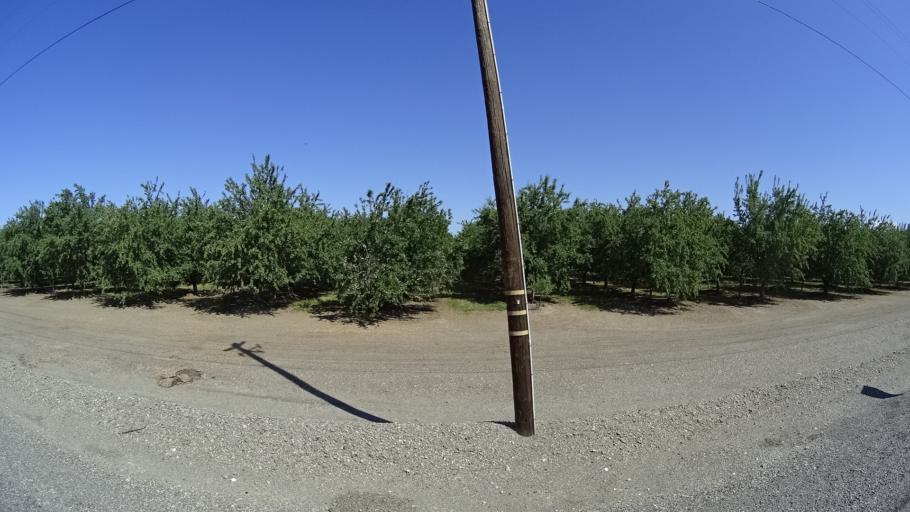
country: US
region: California
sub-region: Glenn County
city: Hamilton City
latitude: 39.7104
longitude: -122.1017
